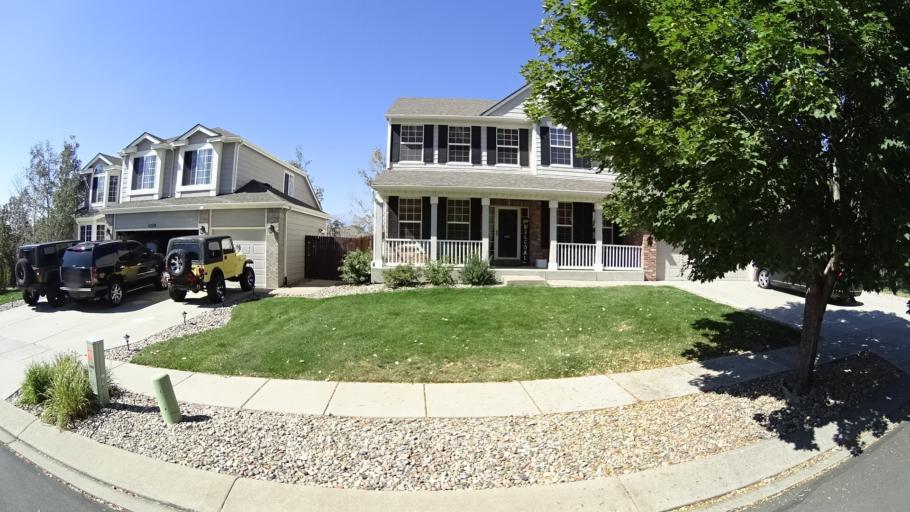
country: US
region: Colorado
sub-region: El Paso County
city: Cimarron Hills
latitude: 38.8961
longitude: -104.7036
